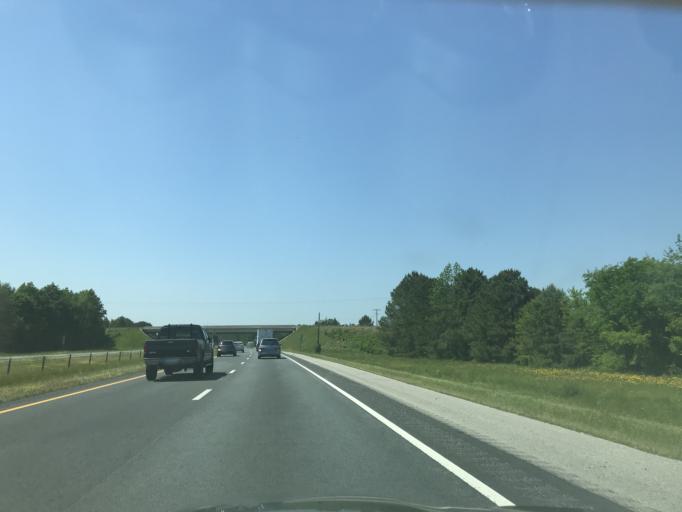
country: US
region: North Carolina
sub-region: Johnston County
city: Benson
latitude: 35.3660
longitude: -78.4919
